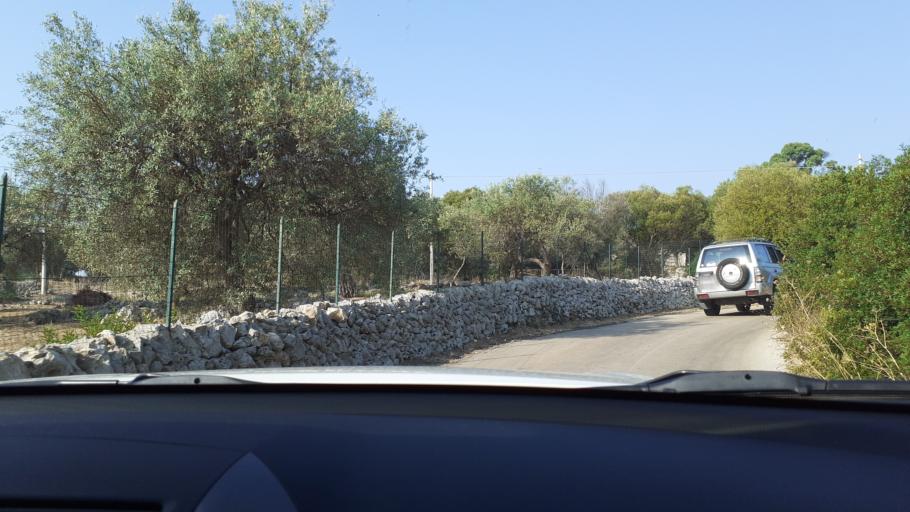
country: IT
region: Sicily
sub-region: Provincia di Siracusa
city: Cassibile
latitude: 36.9759
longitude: 15.1585
